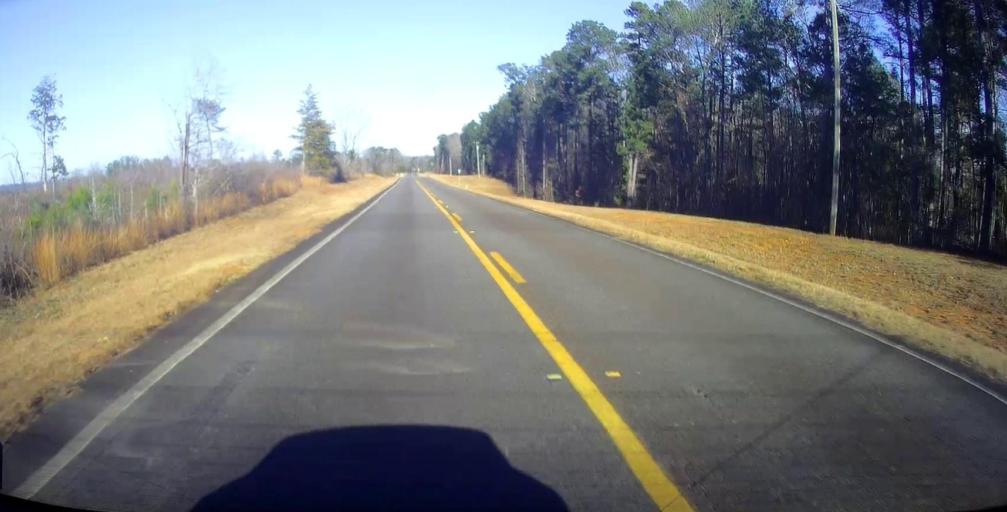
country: US
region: Georgia
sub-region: Talbot County
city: Sardis
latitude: 32.7800
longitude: -84.6642
